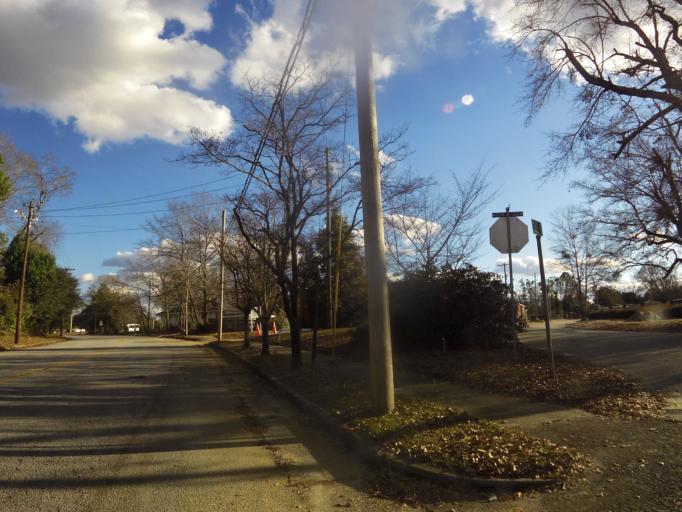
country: US
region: South Carolina
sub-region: Clarendon County
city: Manning
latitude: 33.7033
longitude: -80.2127
